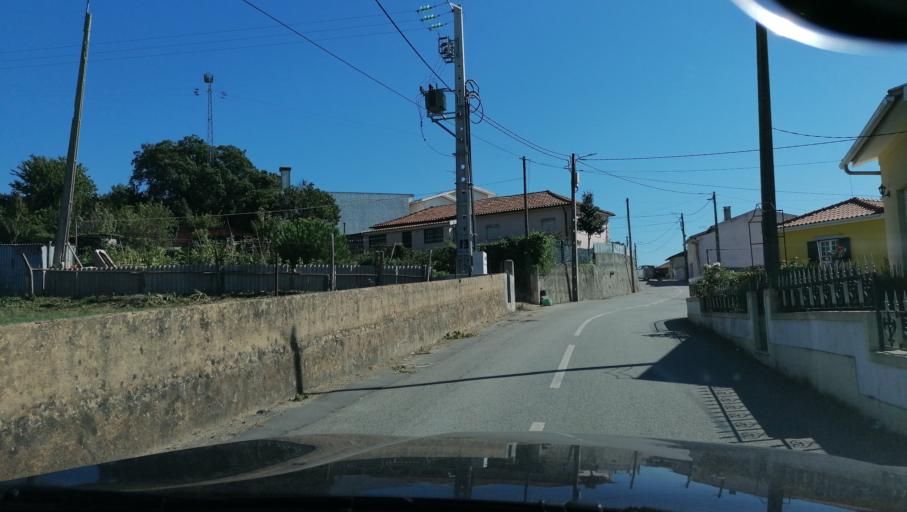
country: PT
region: Aveiro
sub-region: Estarreja
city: Beduido
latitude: 40.7529
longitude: -8.5586
